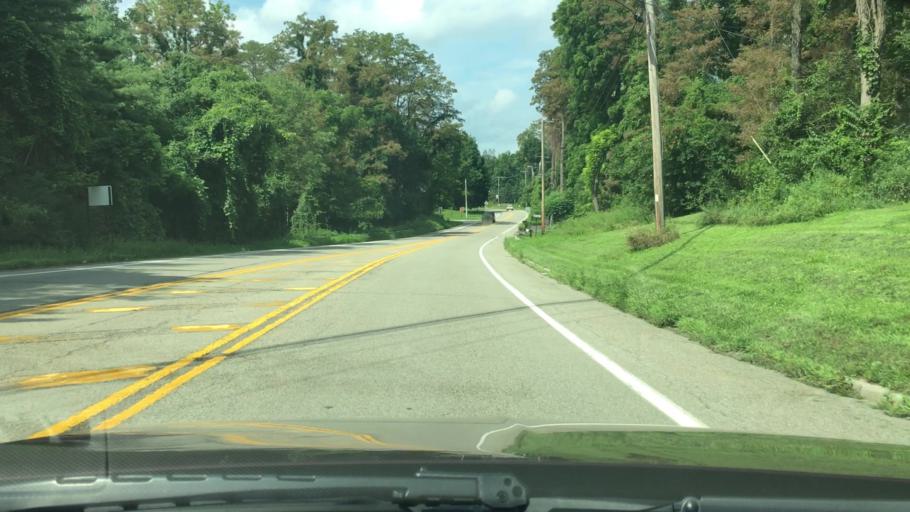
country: US
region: New York
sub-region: Dutchess County
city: Brinckerhoff
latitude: 41.5469
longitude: -73.8202
